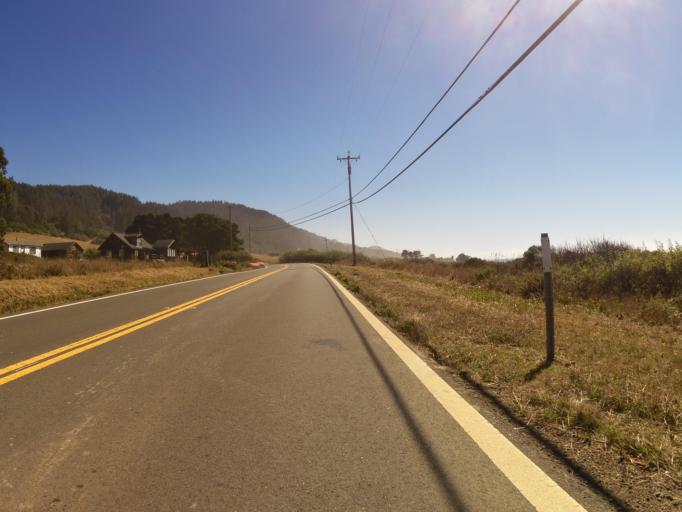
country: US
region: California
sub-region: Mendocino County
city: Fort Bragg
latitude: 39.6456
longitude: -123.7844
